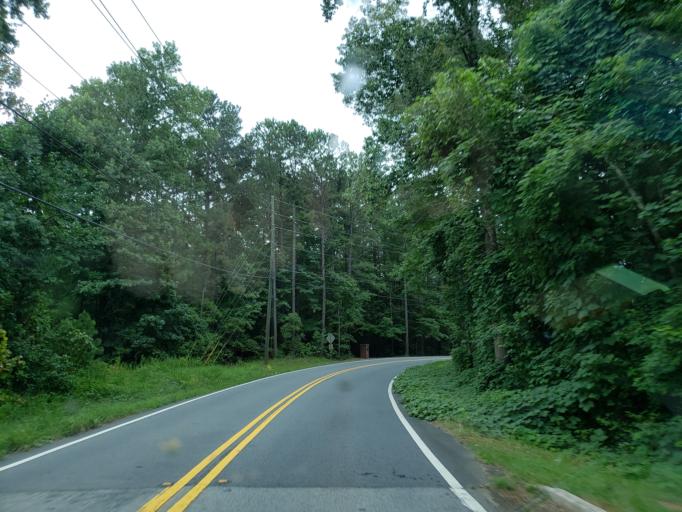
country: US
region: Georgia
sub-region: Cobb County
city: Acworth
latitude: 34.0302
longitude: -84.7394
